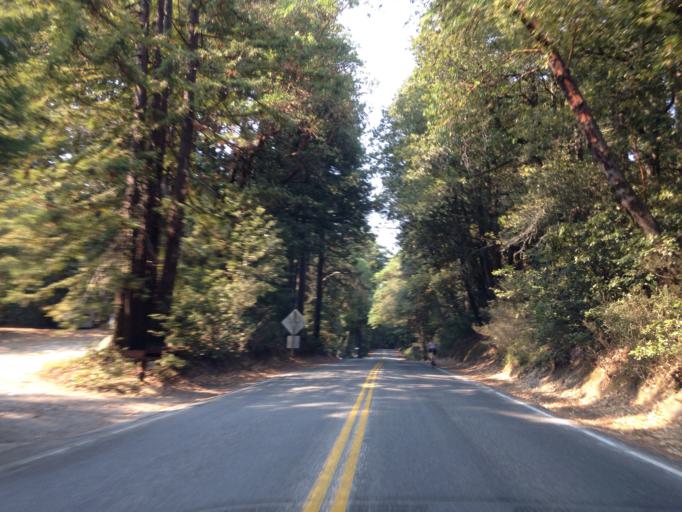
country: US
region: California
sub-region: San Mateo County
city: Emerald Lake Hills
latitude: 37.4373
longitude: -122.3218
